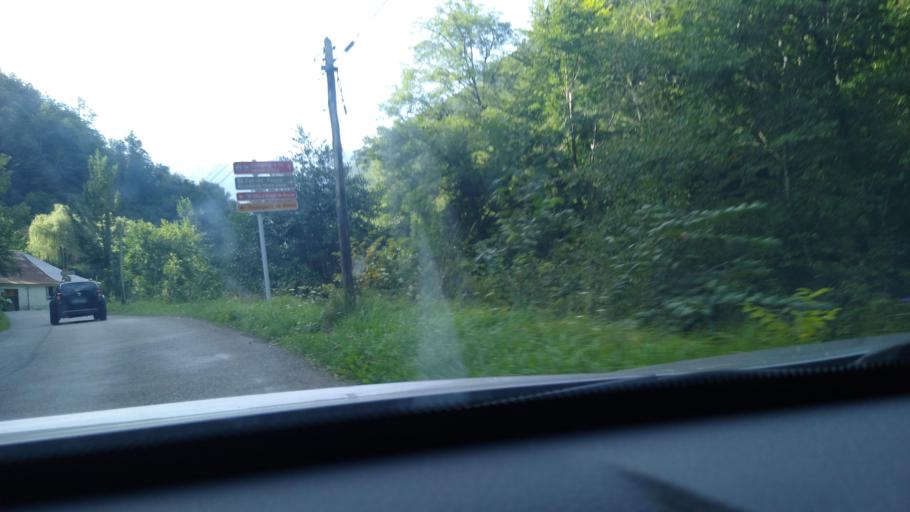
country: FR
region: Midi-Pyrenees
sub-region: Departement de l'Ariege
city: Saint-Girons
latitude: 42.7909
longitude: 1.1857
